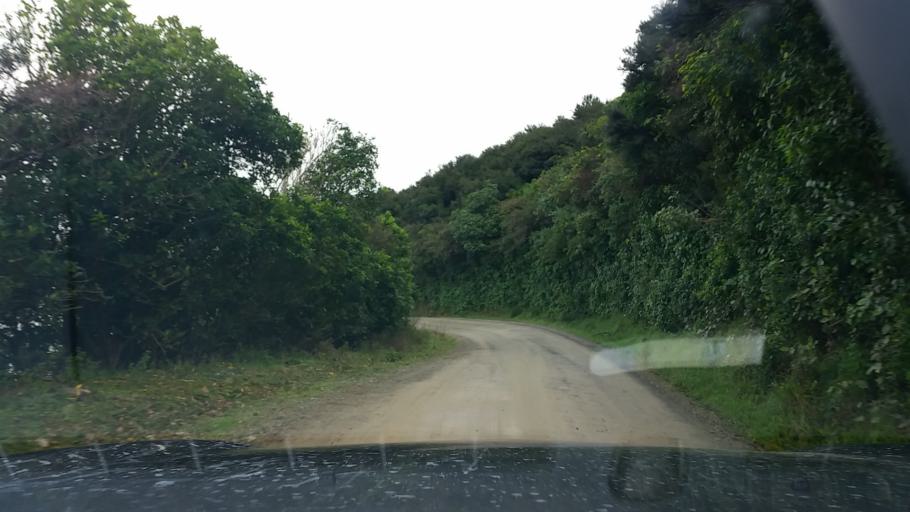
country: NZ
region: Marlborough
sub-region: Marlborough District
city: Picton
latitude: -41.1754
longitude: 174.0483
